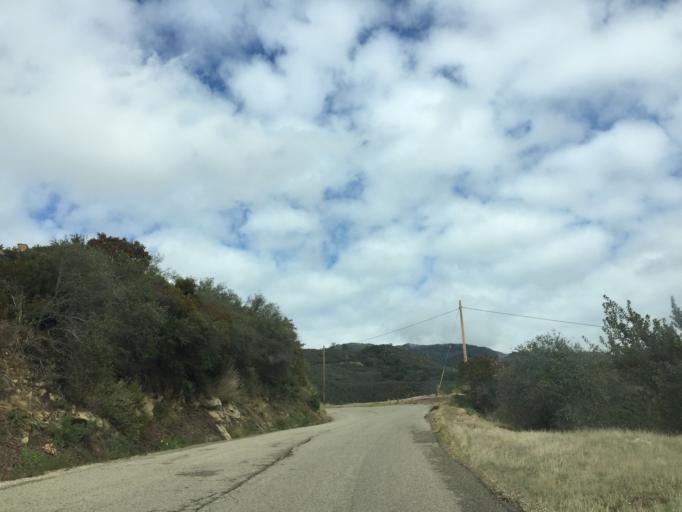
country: US
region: California
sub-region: Santa Barbara County
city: Goleta
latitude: 34.4837
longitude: -119.7981
